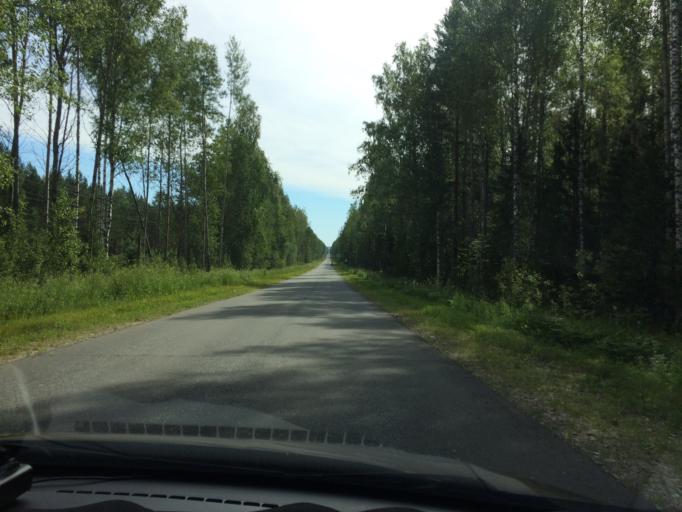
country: RU
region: Mariy-El
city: Mochalishche
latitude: 56.5488
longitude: 48.3306
